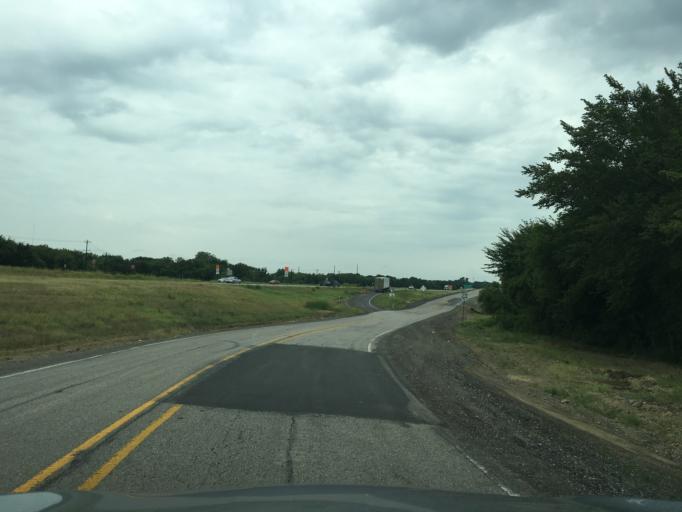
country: US
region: Texas
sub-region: Grayson County
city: Van Alstyne
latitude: 33.3829
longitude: -96.5799
